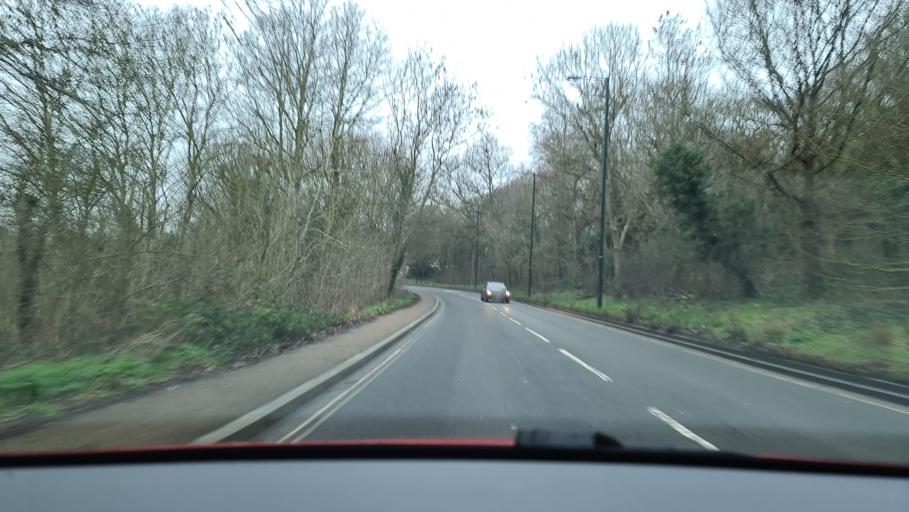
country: GB
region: England
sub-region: Greater London
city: Richmond
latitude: 51.4491
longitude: -0.2992
